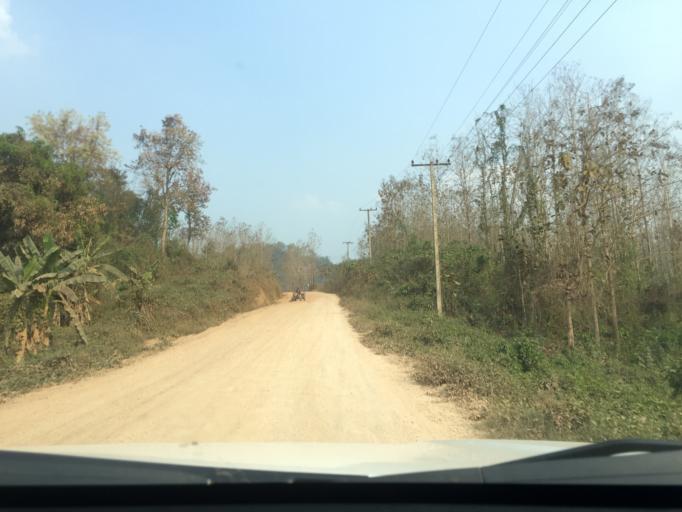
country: LA
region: Xiagnabouli
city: Sainyabuli
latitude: 19.2104
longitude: 101.6968
